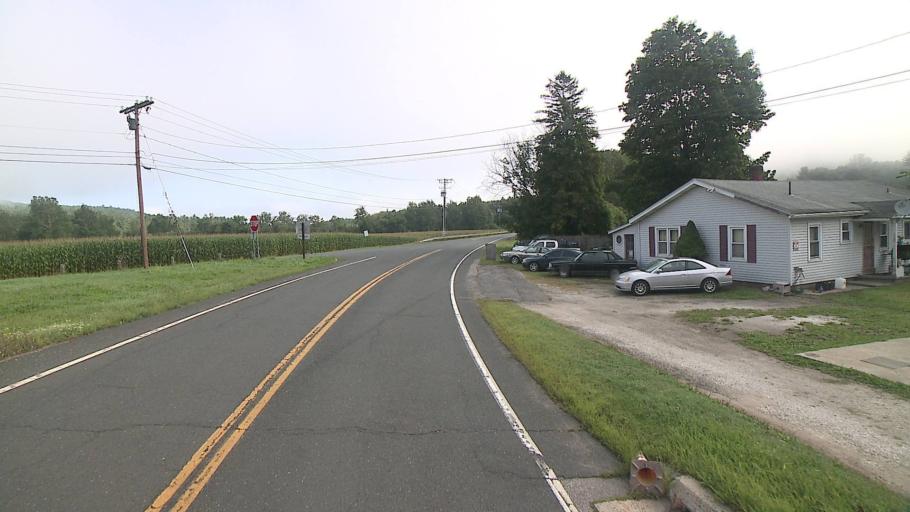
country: US
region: Connecticut
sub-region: Litchfield County
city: Canaan
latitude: 41.9316
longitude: -73.3642
